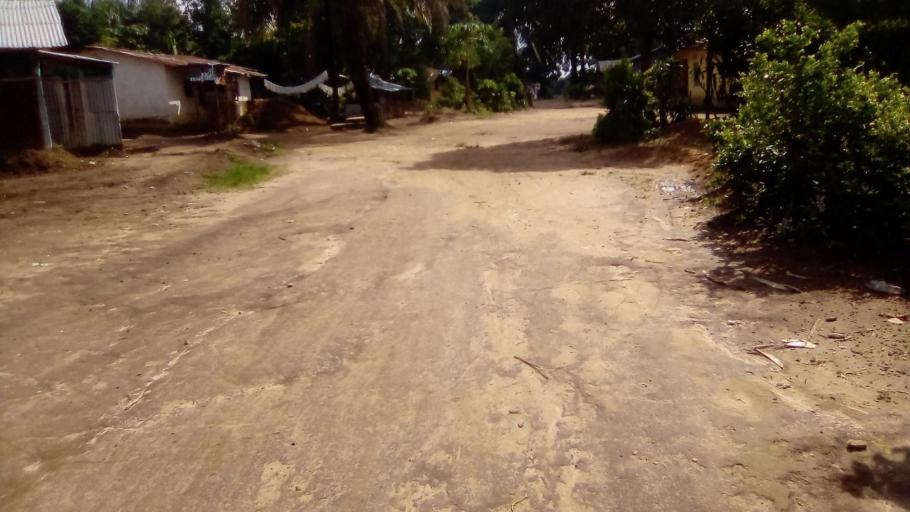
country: SL
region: Southern Province
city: Bo
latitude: 7.9757
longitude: -11.7259
